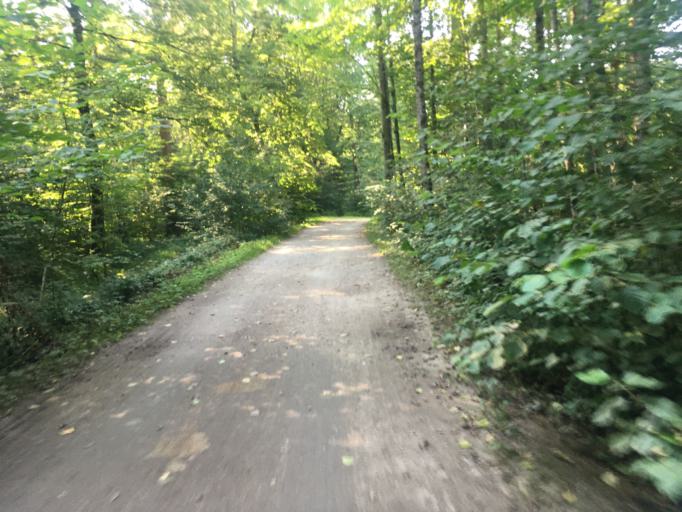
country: CH
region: Bern
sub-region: Emmental District
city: Oberburg
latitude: 47.0332
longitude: 7.6383
